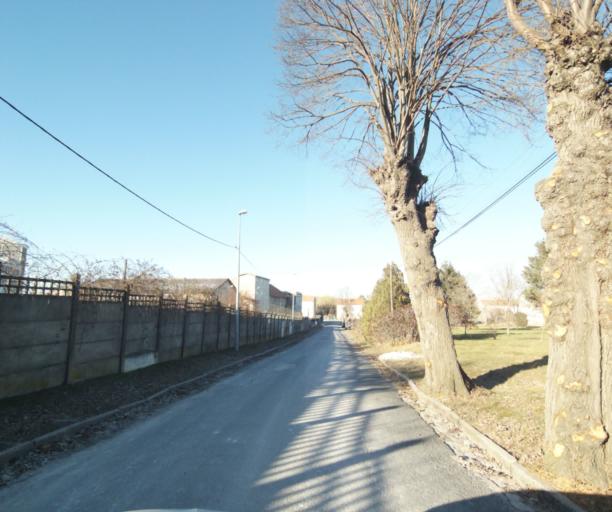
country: FR
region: Lorraine
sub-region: Departement de Meurthe-et-Moselle
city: Art-sur-Meurthe
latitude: 48.6389
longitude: 6.2685
